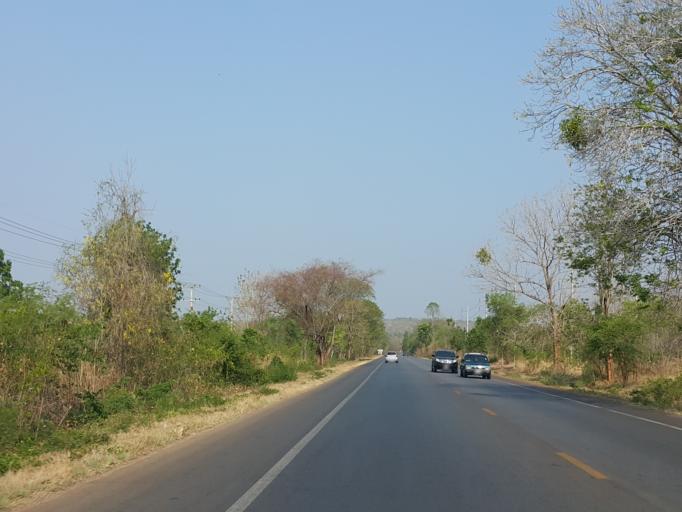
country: TH
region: Kanchanaburi
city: Sai Yok
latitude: 14.0973
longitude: 99.2444
